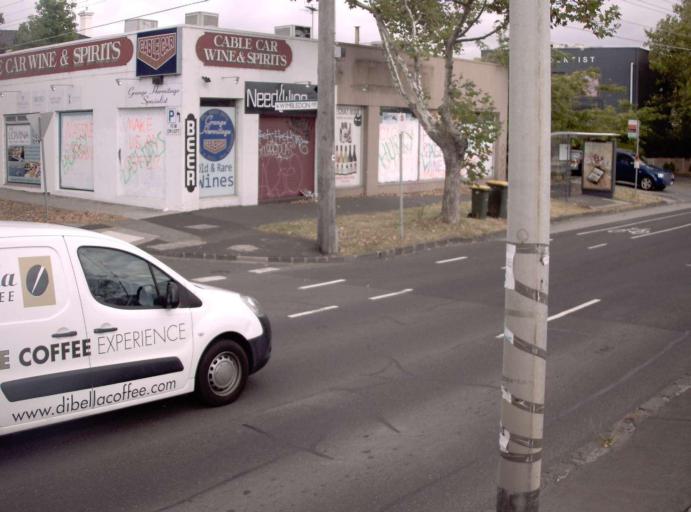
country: AU
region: Victoria
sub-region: Port Phillip
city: Balaclava
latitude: -37.8726
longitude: 144.9898
